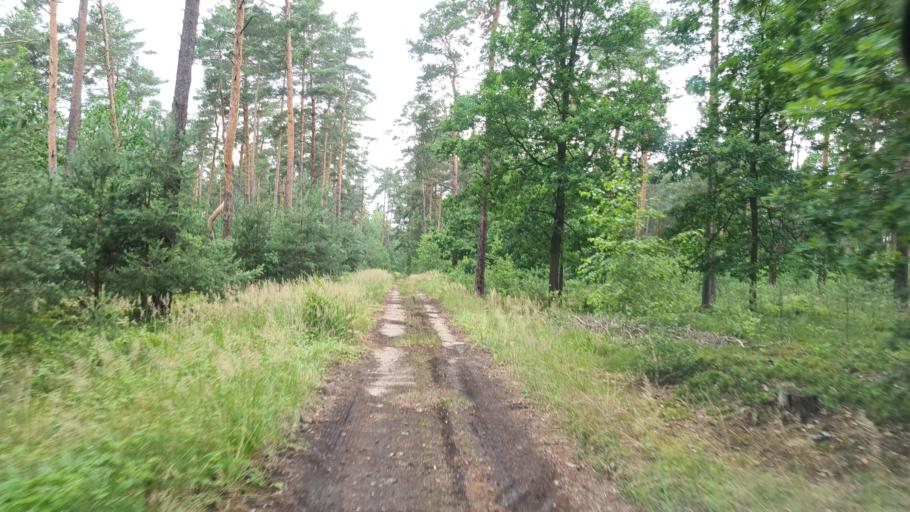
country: DE
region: Brandenburg
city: Crinitz
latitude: 51.7181
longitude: 13.7334
